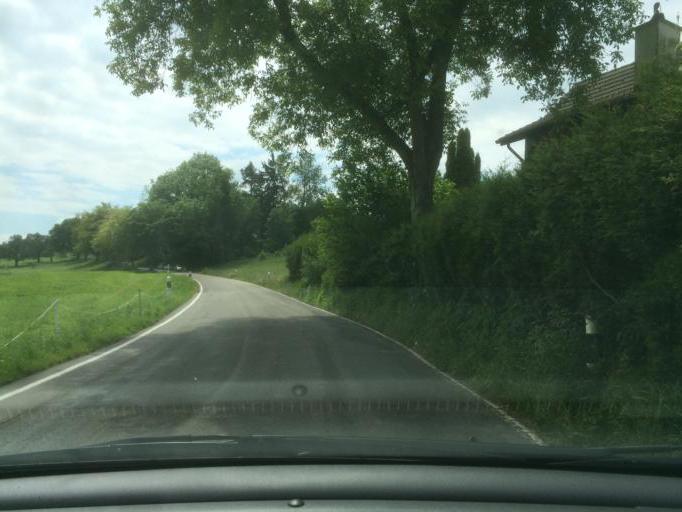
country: CH
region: Zurich
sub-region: Bezirk Pfaeffikon
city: Pfaeffikon / Pfaeffikon (Dorfkern)
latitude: 47.3582
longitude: 8.7657
